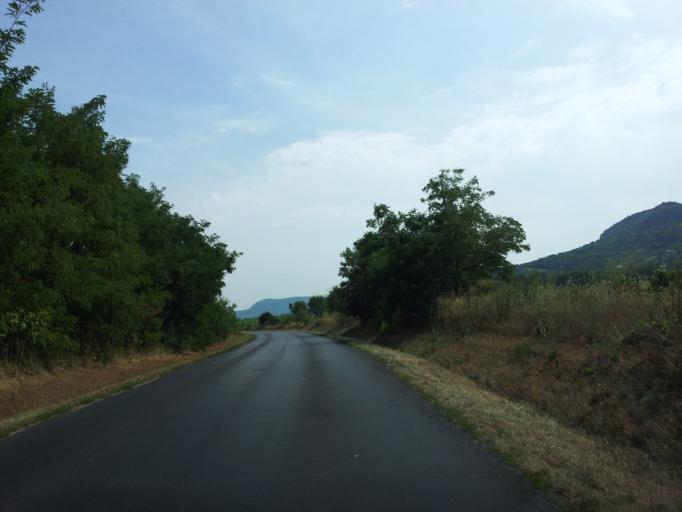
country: HU
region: Veszprem
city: Tapolca
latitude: 46.8605
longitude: 17.4543
